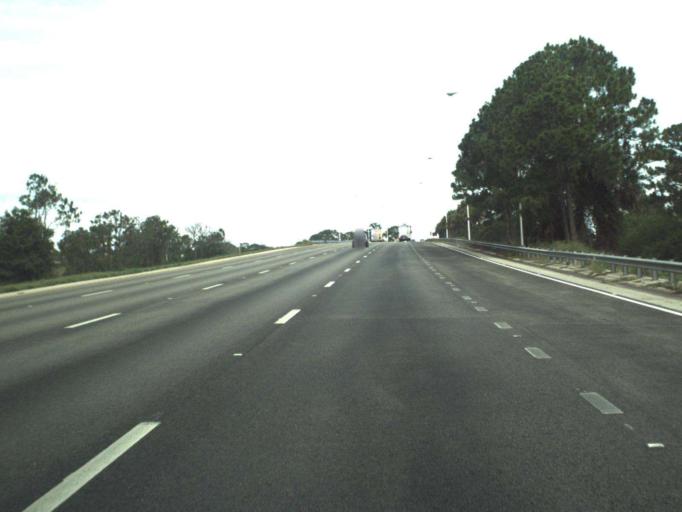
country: US
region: Florida
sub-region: Saint Lucie County
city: Lakewood Park
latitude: 27.4682
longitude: -80.4230
